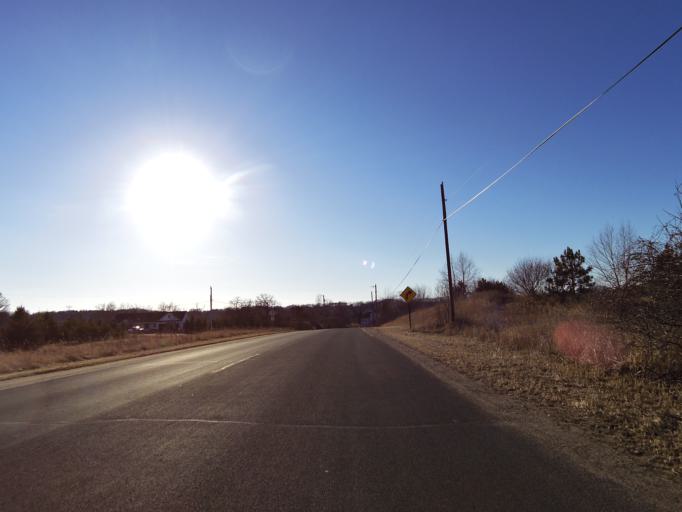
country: US
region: Minnesota
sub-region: Washington County
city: Lakeland
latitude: 44.9761
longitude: -92.8004
